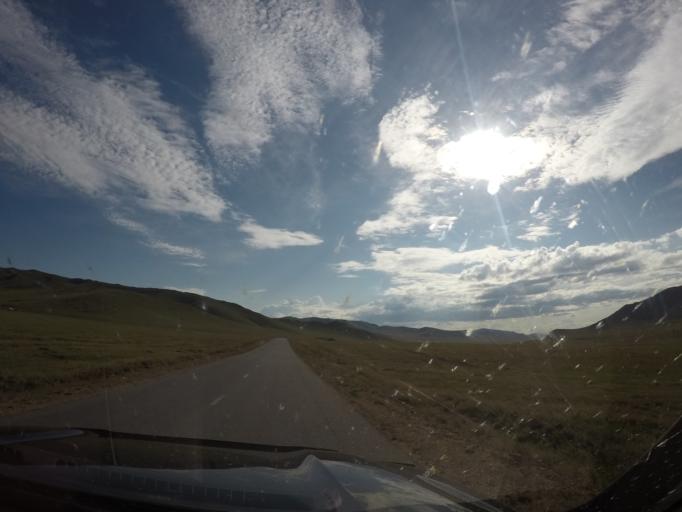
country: MN
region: Central Aimak
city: Bayandelger
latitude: 47.7012
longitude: 108.5571
